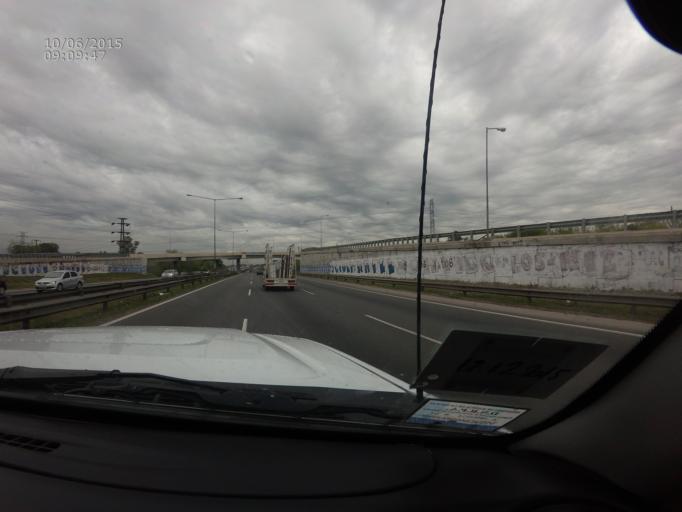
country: AR
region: Buenos Aires
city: Belen de Escobar
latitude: -34.3738
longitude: -58.7599
